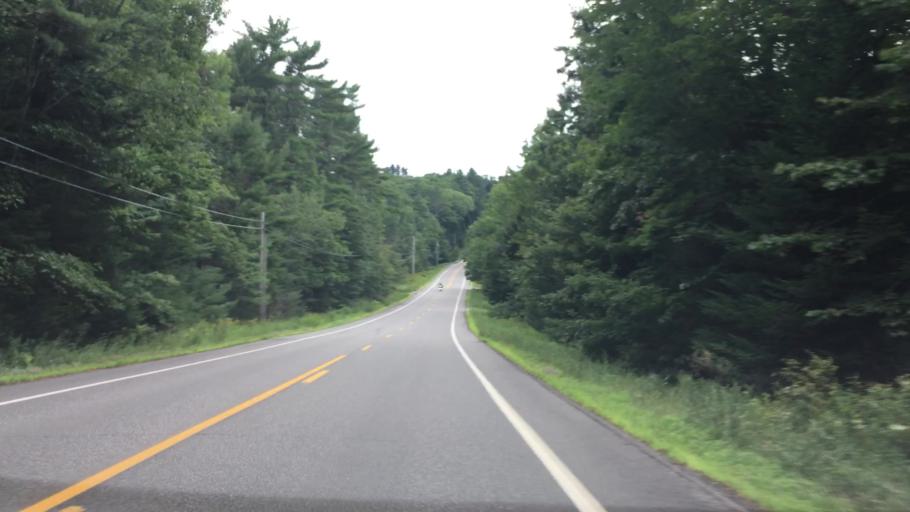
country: US
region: Maine
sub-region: Waldo County
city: Lincolnville
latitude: 44.3317
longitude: -69.0592
